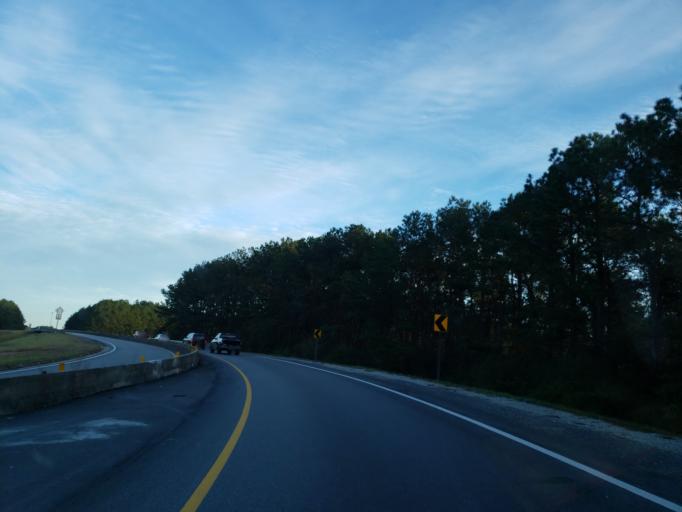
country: US
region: Mississippi
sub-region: Lamar County
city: West Hattiesburg
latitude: 31.2407
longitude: -89.3260
